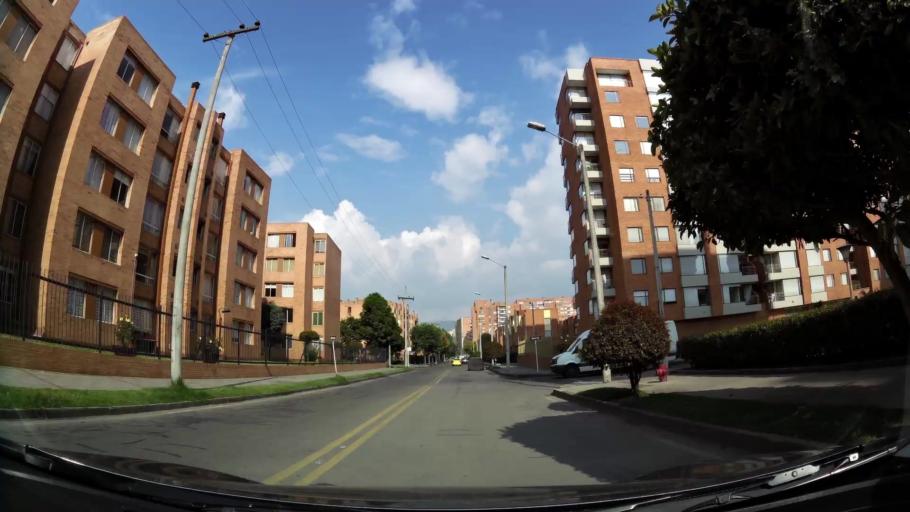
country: CO
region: Bogota D.C.
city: Barrio San Luis
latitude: 4.7346
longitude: -74.0606
